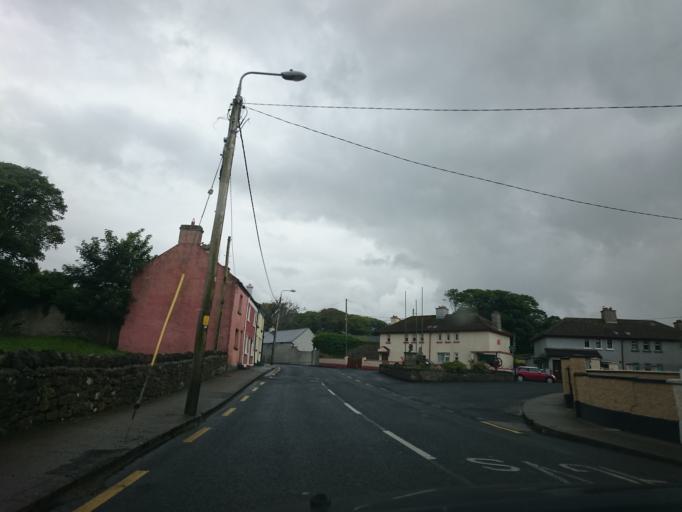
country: IE
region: Connaught
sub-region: Maigh Eo
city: Ballina
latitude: 54.2118
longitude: -9.2195
